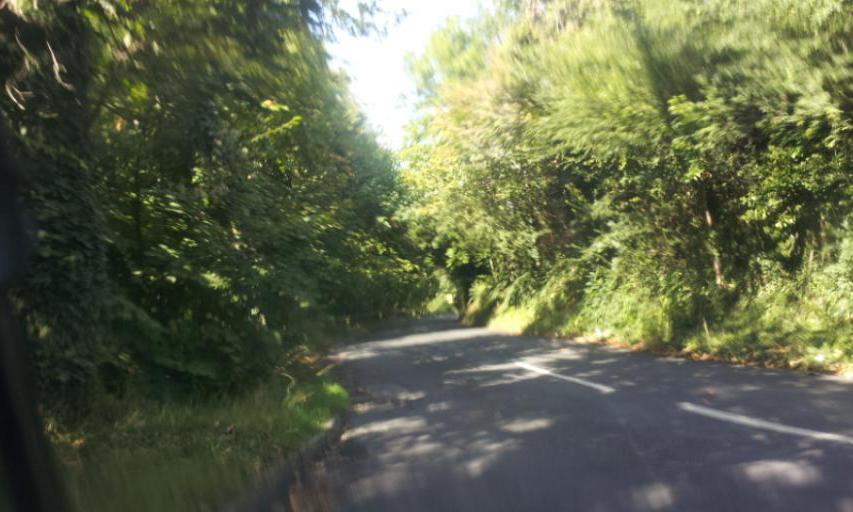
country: GB
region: England
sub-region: Kent
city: Gillingham
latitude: 51.3679
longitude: 0.5526
